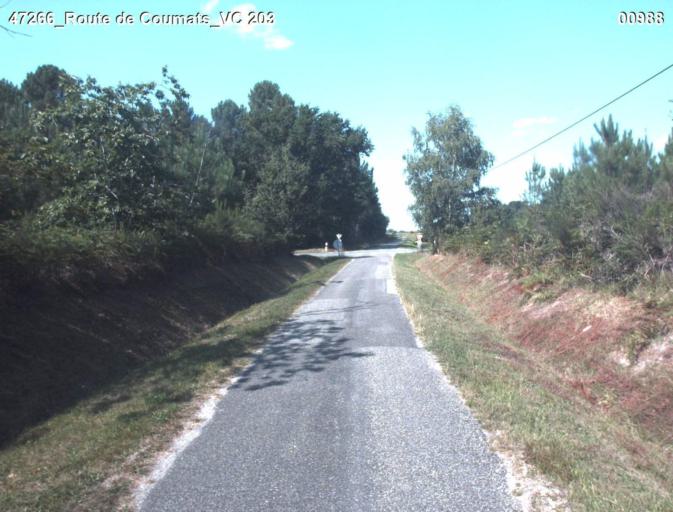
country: FR
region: Aquitaine
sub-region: Departement des Landes
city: Gabarret
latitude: 44.0092
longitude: 0.0917
